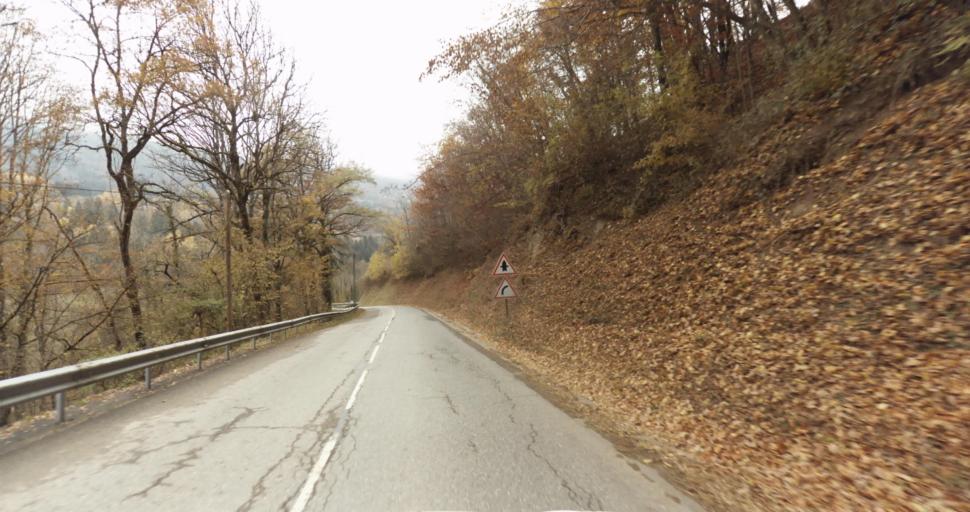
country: FR
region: Rhone-Alpes
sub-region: Departement de la Haute-Savoie
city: Saint-Jorioz
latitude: 45.8023
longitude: 6.1481
